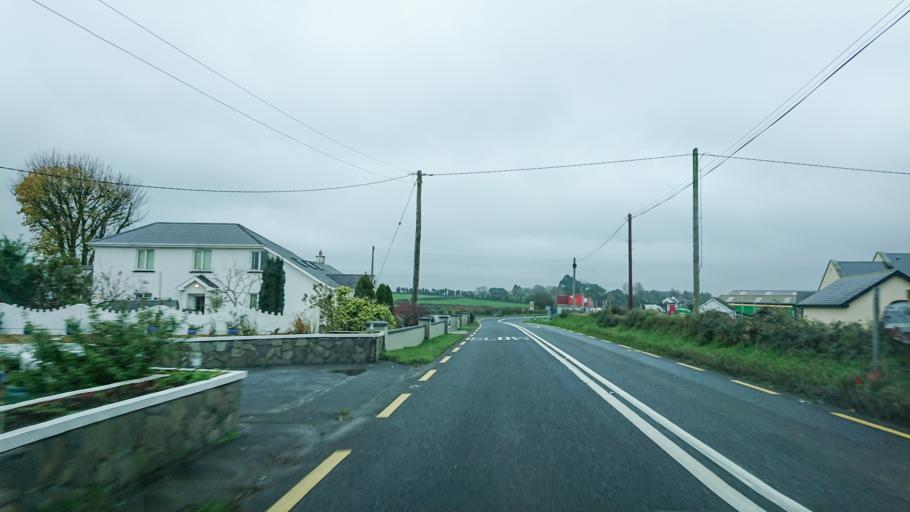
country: IE
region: Leinster
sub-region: Kilkenny
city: Mooncoin
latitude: 52.3013
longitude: -7.2716
